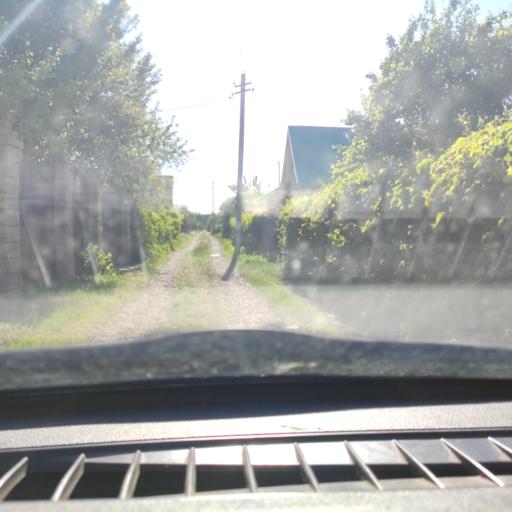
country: RU
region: Samara
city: Tol'yatti
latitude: 53.6273
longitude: 49.4048
